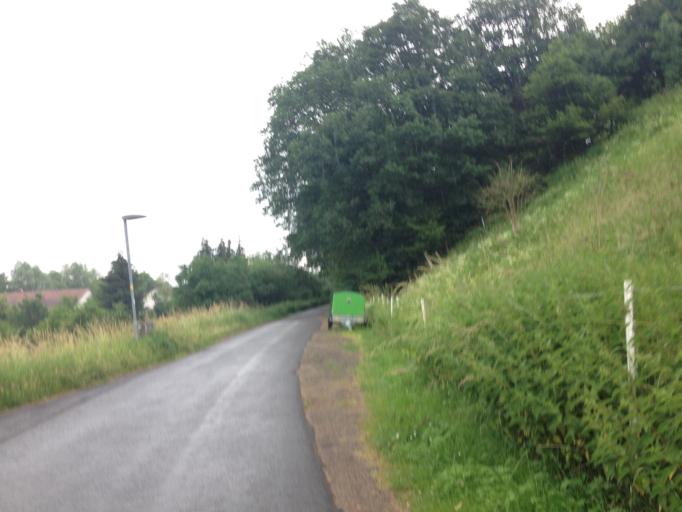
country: DE
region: Hesse
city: Wetter
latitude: 50.8630
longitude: 8.7376
